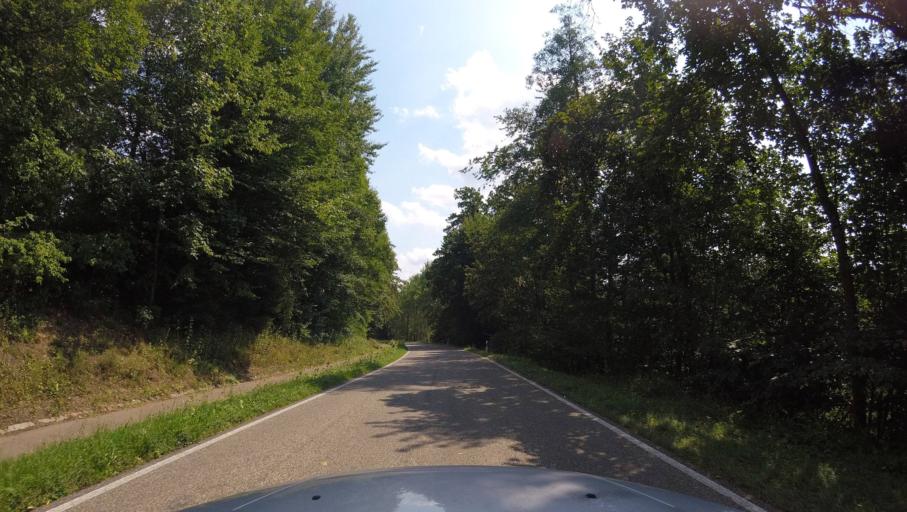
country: DE
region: Baden-Wuerttemberg
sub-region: Regierungsbezirk Stuttgart
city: Kaisersbach
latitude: 48.9155
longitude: 9.6708
